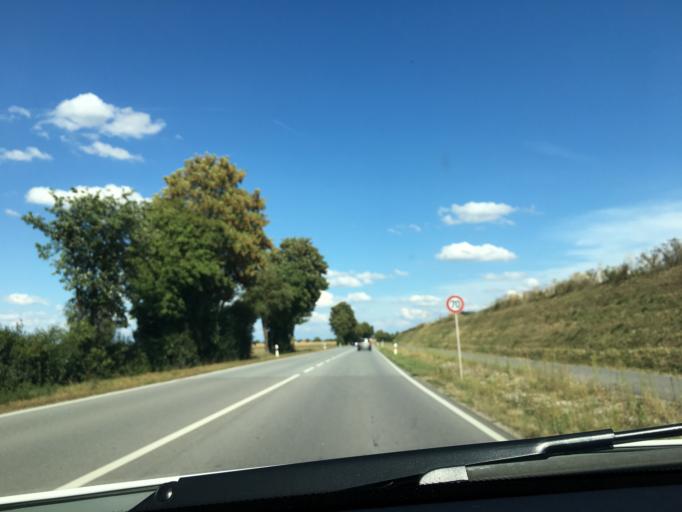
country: DE
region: Bavaria
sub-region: Lower Bavaria
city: Dingolfing
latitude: 48.6493
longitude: 12.5099
